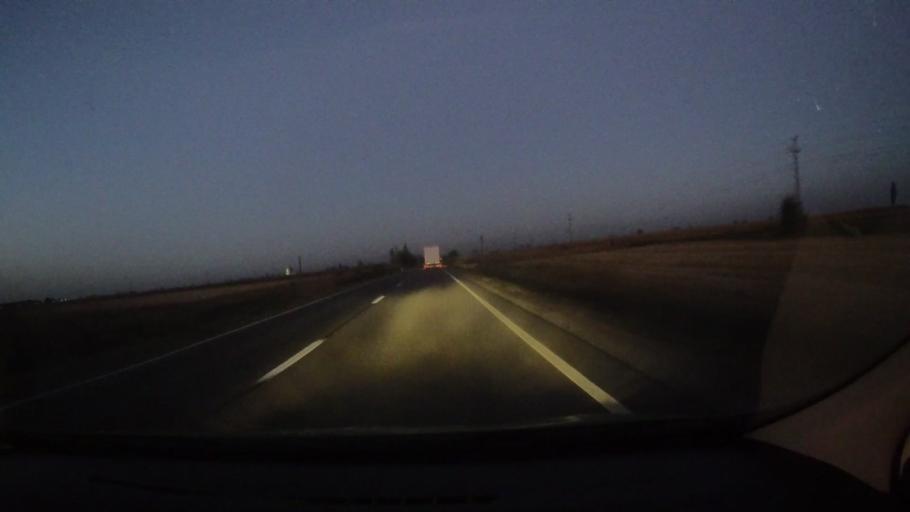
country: RO
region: Bihor
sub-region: Comuna Curtuiuseni
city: Curtuiseni
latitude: 47.5304
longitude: 22.1937
